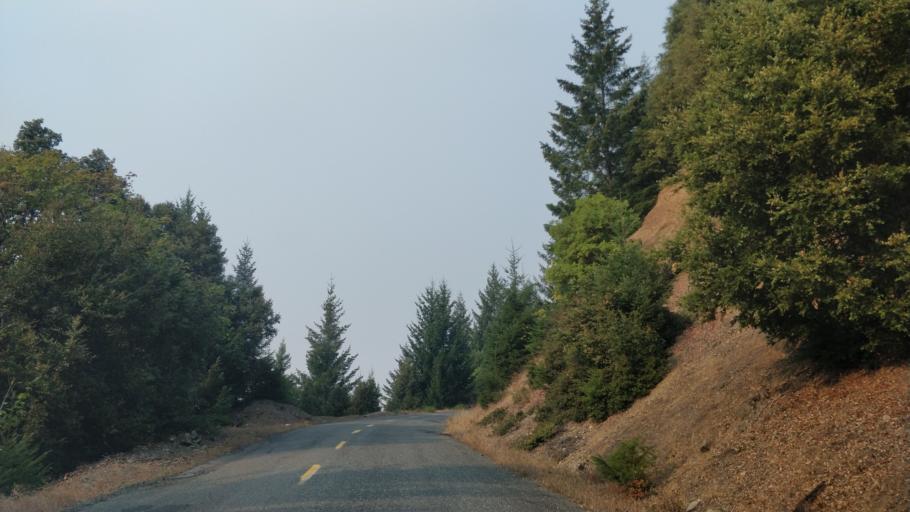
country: US
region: California
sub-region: Humboldt County
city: Rio Dell
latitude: 40.2557
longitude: -124.1175
